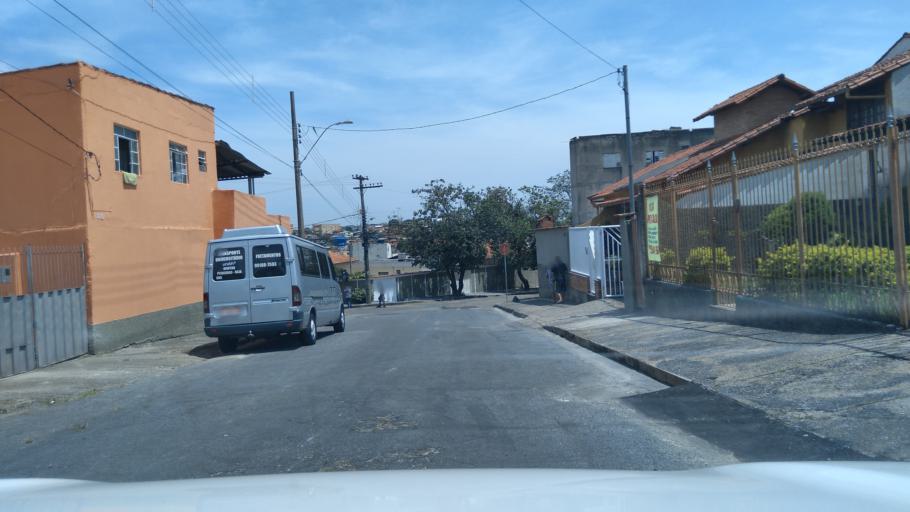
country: BR
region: Minas Gerais
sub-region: Contagem
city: Contagem
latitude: -19.9009
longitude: -44.0146
